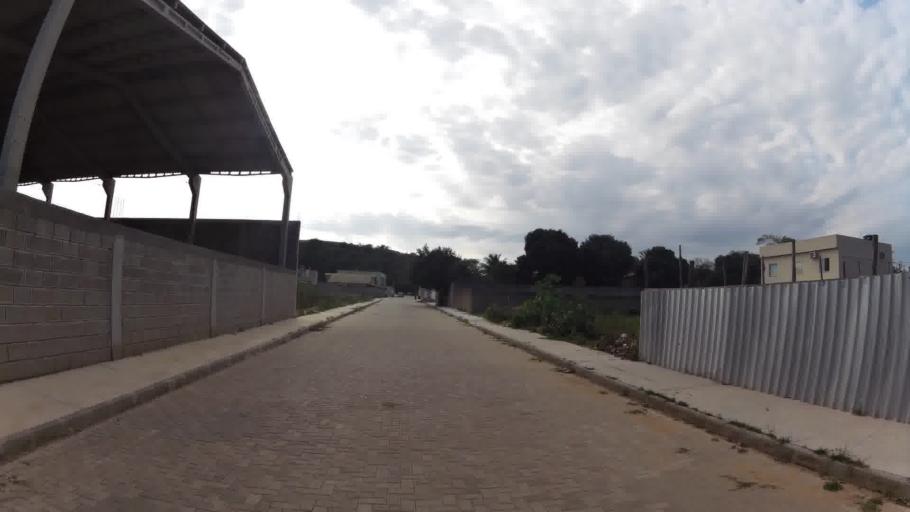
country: BR
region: Espirito Santo
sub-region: Itapemirim
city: Itapemirim
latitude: -21.0083
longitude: -40.8289
